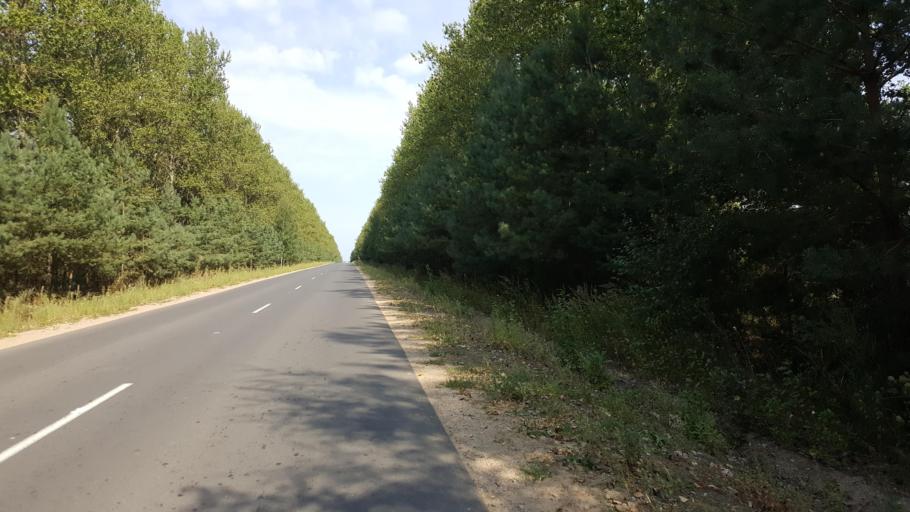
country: BY
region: Brest
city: Kamyanyets
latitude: 52.4463
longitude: 23.7383
